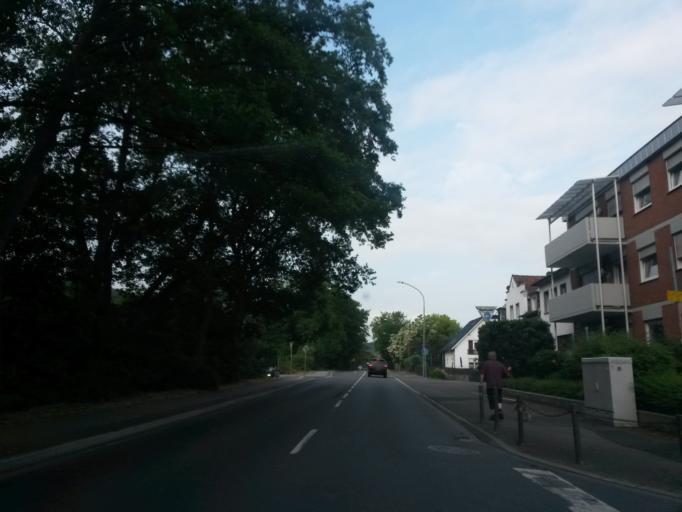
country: DE
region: North Rhine-Westphalia
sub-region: Regierungsbezirk Koln
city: Overath
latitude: 50.9590
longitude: 7.2366
